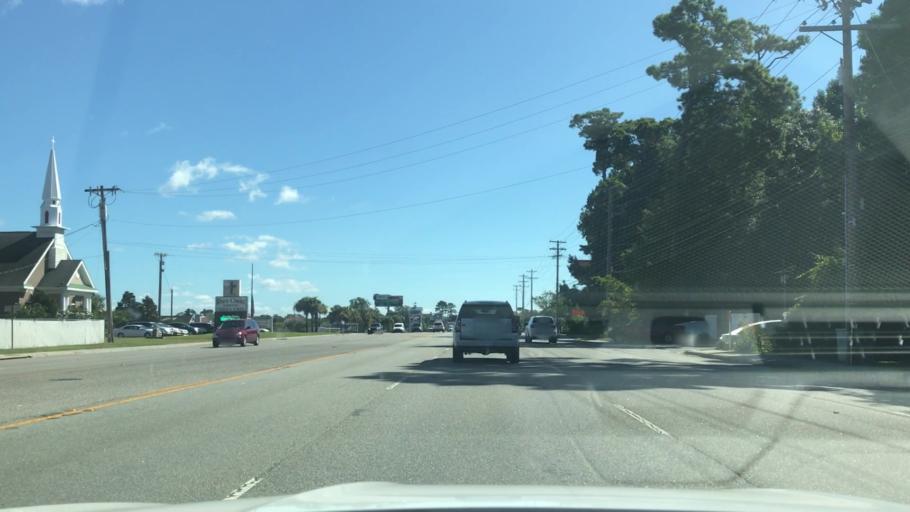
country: US
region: South Carolina
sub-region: Horry County
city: North Myrtle Beach
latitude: 33.7958
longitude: -78.7481
